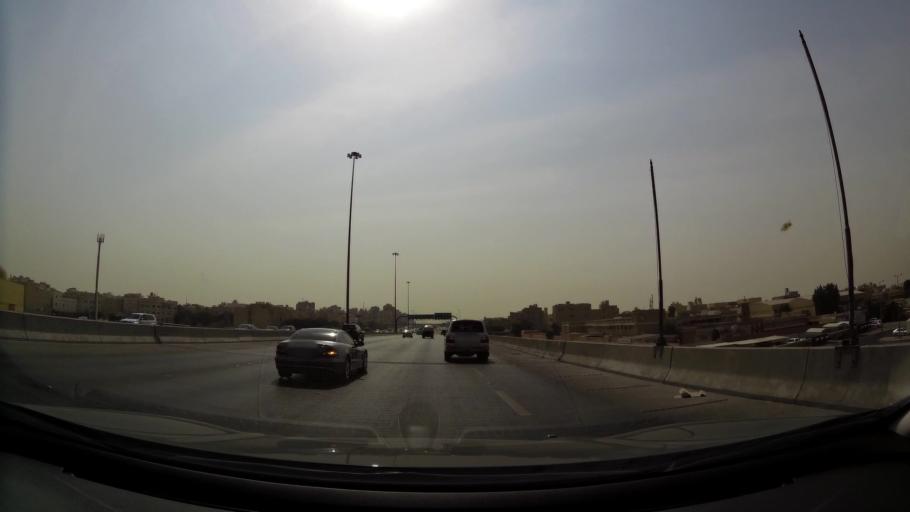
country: KW
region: Al Farwaniyah
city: Al Farwaniyah
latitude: 29.2888
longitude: 47.9477
